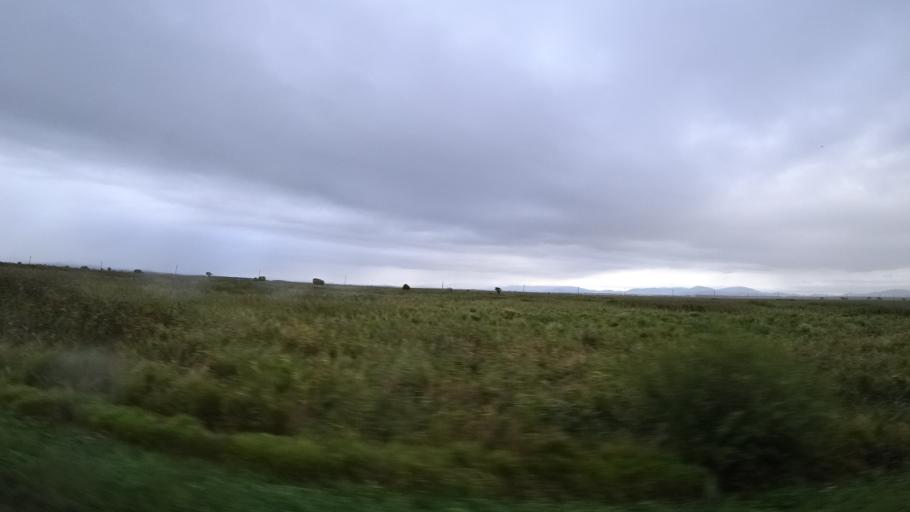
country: RU
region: Primorskiy
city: Chernigovka
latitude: 44.3884
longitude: 132.5294
